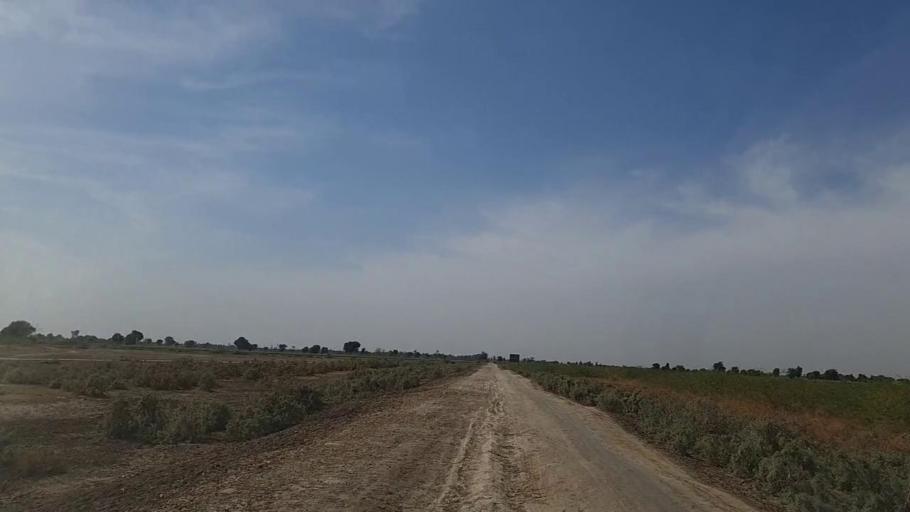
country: PK
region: Sindh
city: Samaro
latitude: 25.2264
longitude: 69.4412
